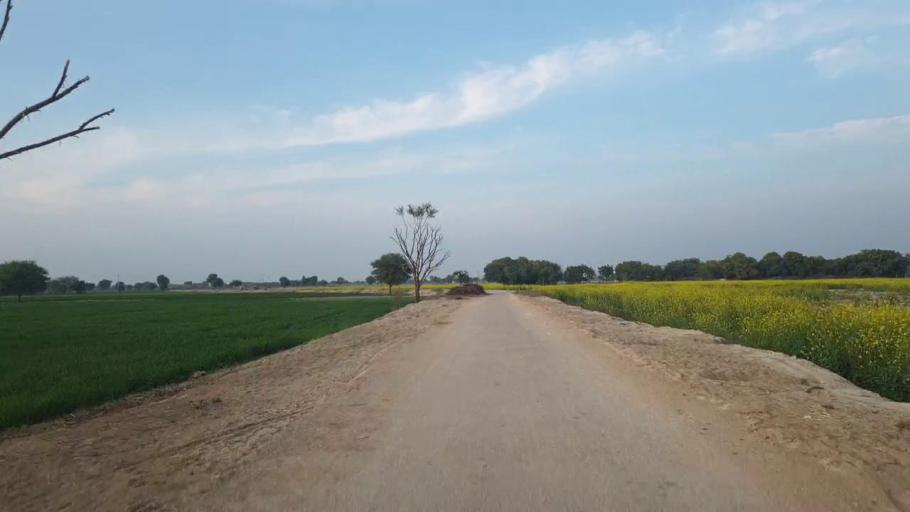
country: PK
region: Sindh
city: Shahpur Chakar
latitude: 26.0983
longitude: 68.5485
